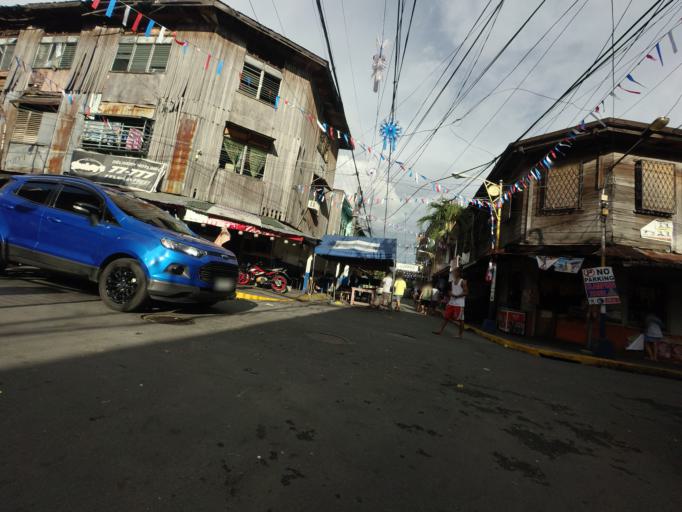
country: PH
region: Metro Manila
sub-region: City of Manila
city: Quiapo
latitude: 14.5890
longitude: 120.9853
